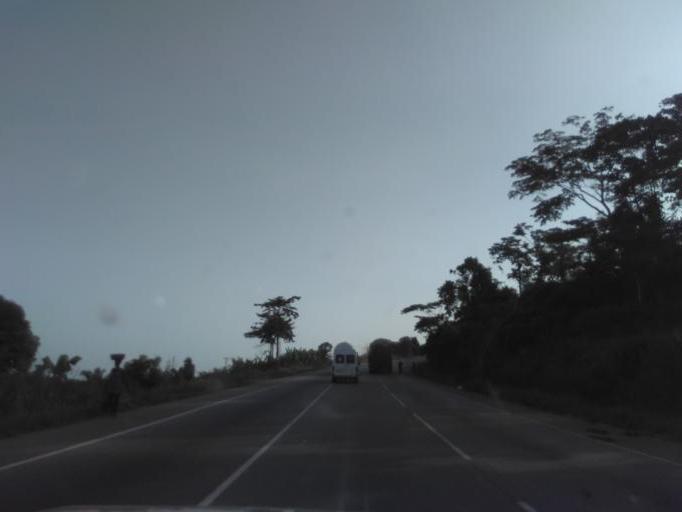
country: GH
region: Ashanti
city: Konongo
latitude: 6.6122
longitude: -1.2381
